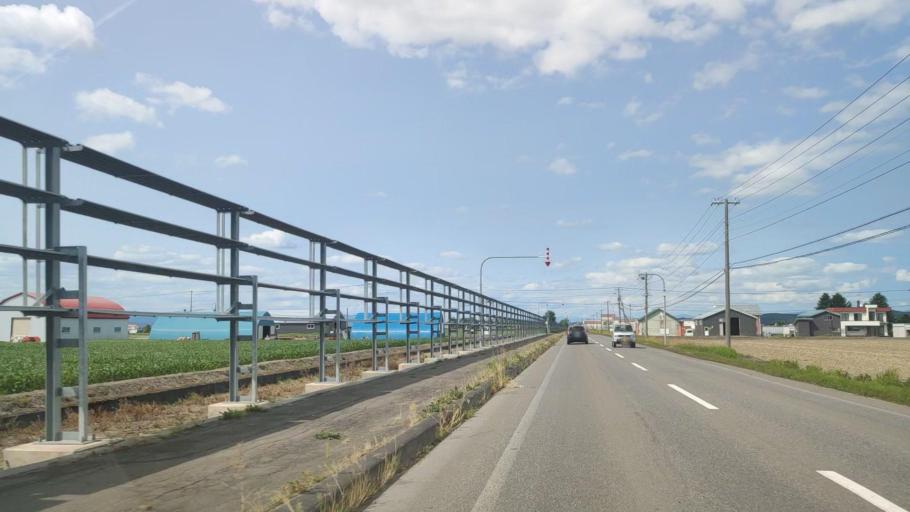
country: JP
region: Hokkaido
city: Nayoro
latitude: 44.1946
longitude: 142.4159
